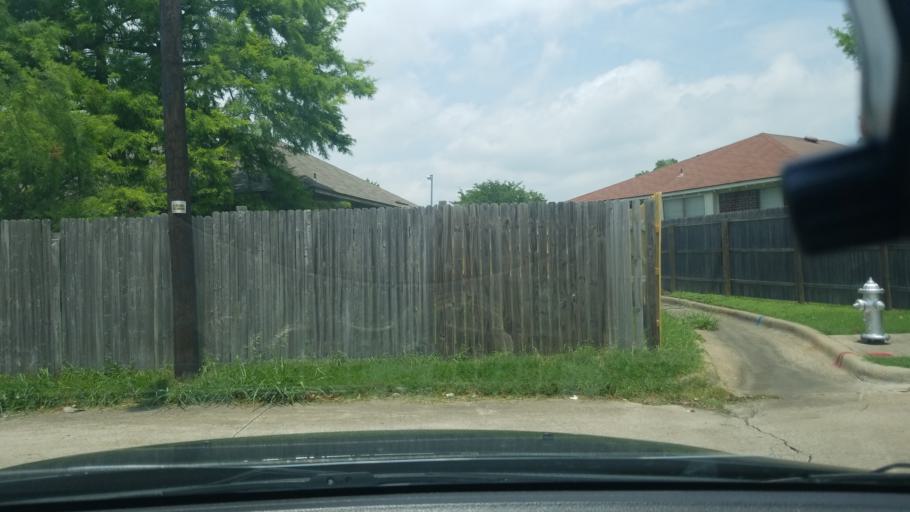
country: US
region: Texas
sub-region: Dallas County
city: Mesquite
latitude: 32.7974
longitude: -96.6154
